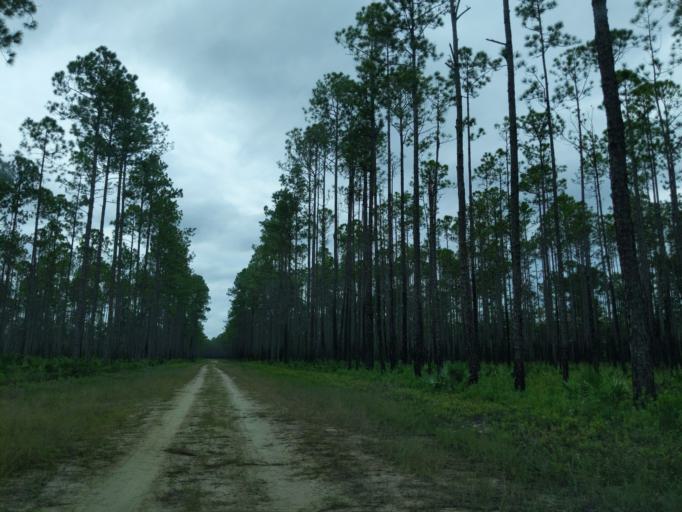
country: US
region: Florida
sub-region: Gadsden County
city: Midway
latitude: 30.3741
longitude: -84.4871
